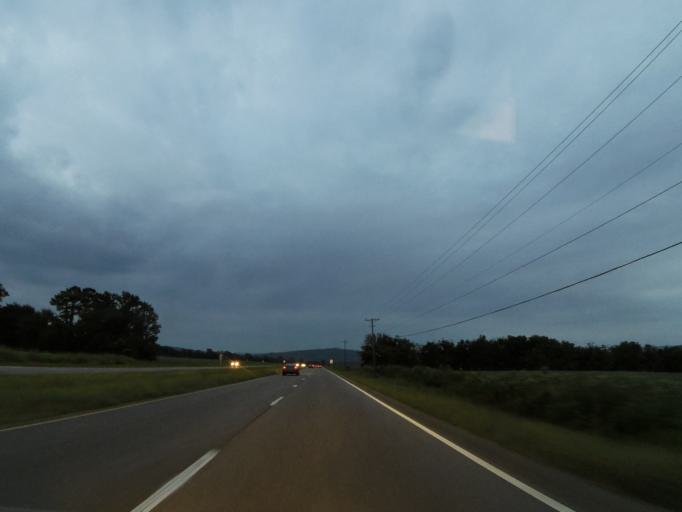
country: US
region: Alabama
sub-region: Madison County
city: Moores Mill
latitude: 34.7348
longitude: -86.4302
